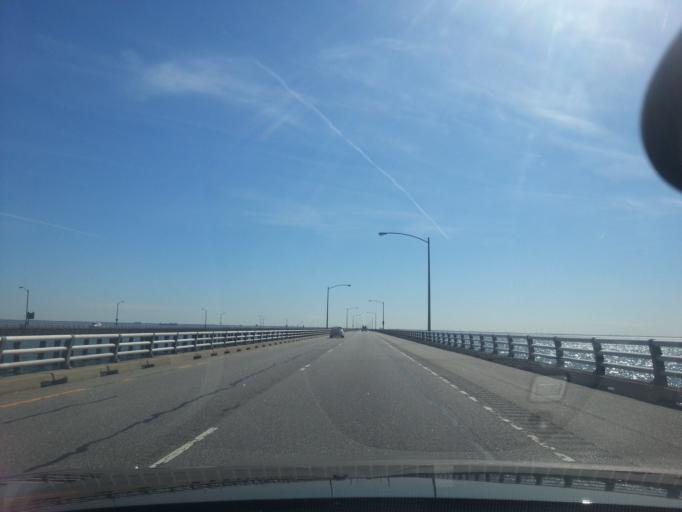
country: US
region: Virginia
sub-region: City of Virginia Beach
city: Virginia Beach
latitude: 37.0259
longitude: -76.0889
